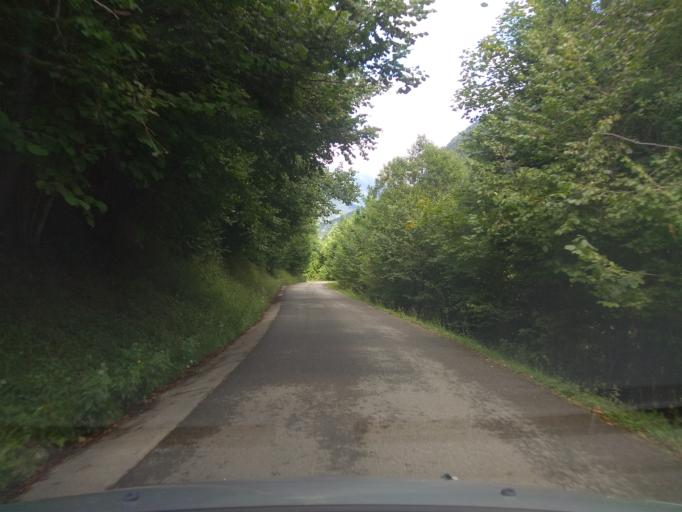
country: ES
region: Catalonia
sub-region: Provincia de Lleida
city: Vielha
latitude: 42.7006
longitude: 0.7108
